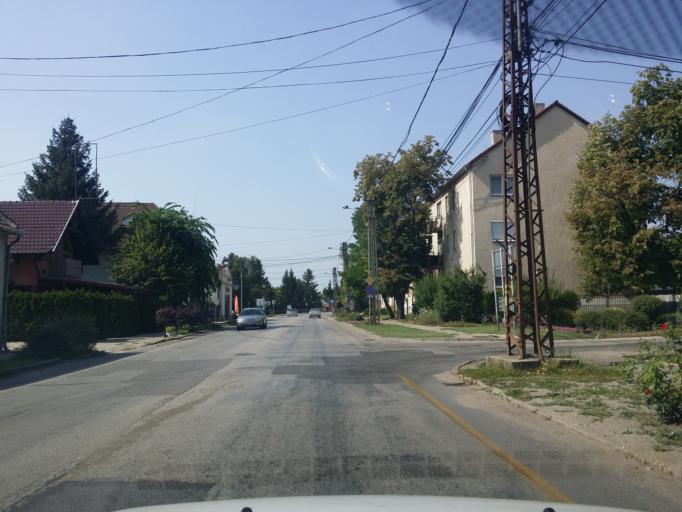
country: HU
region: Fejer
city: Sarbogard
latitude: 46.8877
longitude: 18.6193
